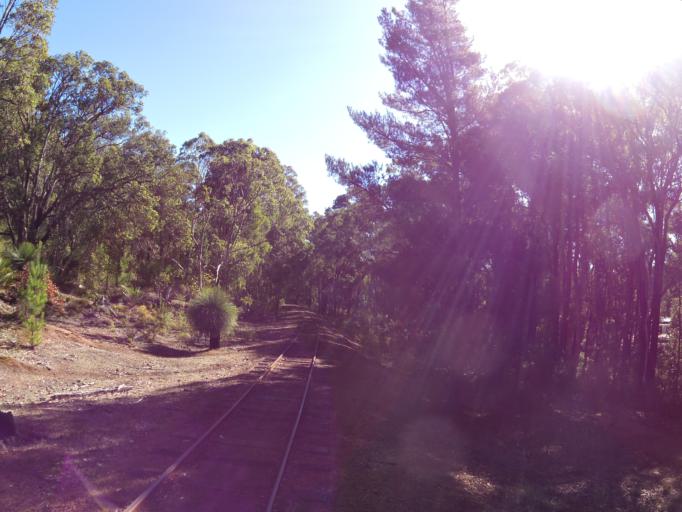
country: AU
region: Western Australia
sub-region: Waroona
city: Waroona
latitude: -32.7122
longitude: 116.0896
